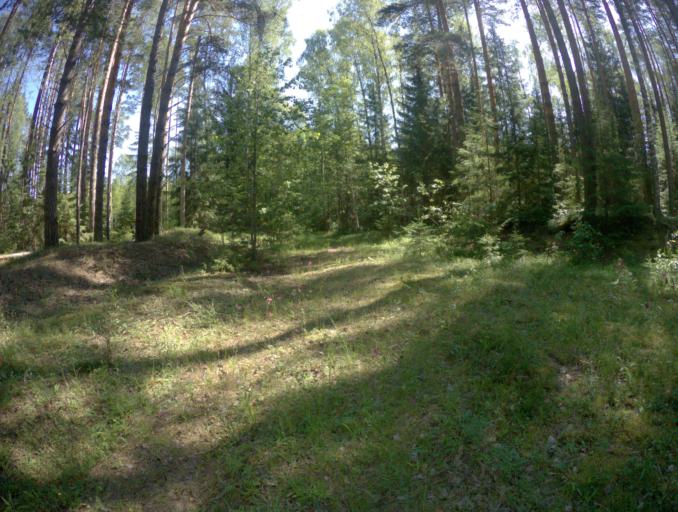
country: RU
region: Vladimir
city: Vyazniki
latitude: 56.3324
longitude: 42.3139
